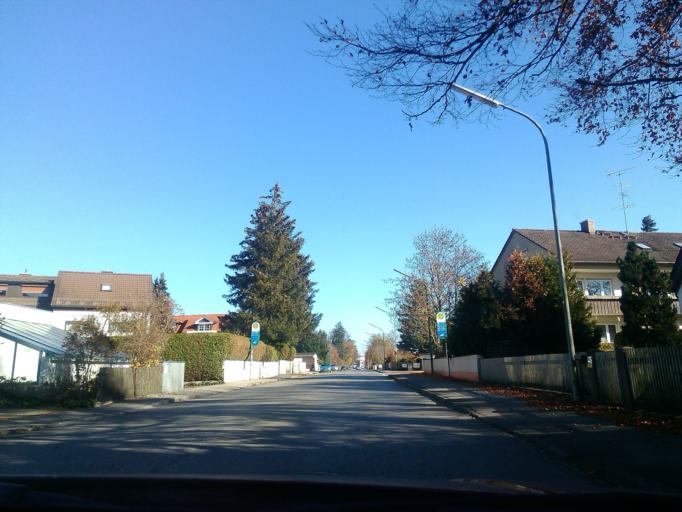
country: DE
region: Bavaria
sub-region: Upper Bavaria
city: Olching
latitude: 48.2139
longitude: 11.3410
